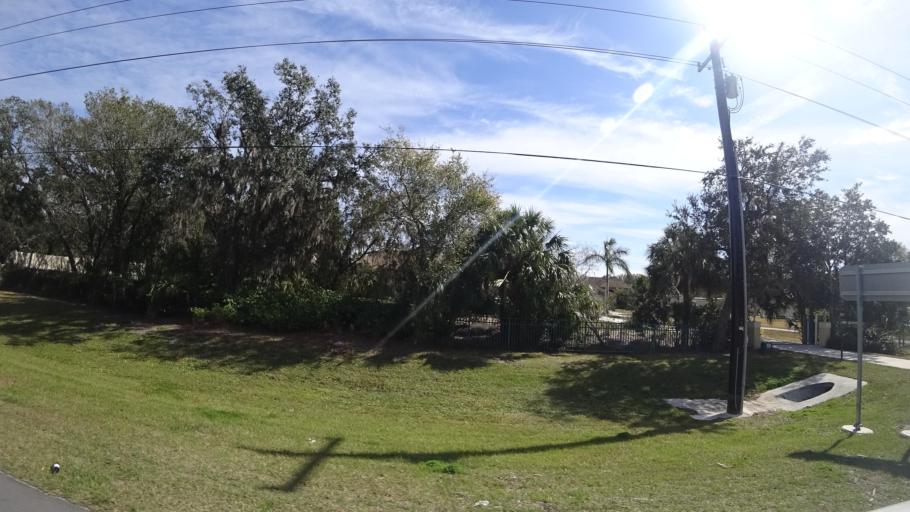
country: US
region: Florida
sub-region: Manatee County
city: Ellenton
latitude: 27.5339
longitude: -82.4264
